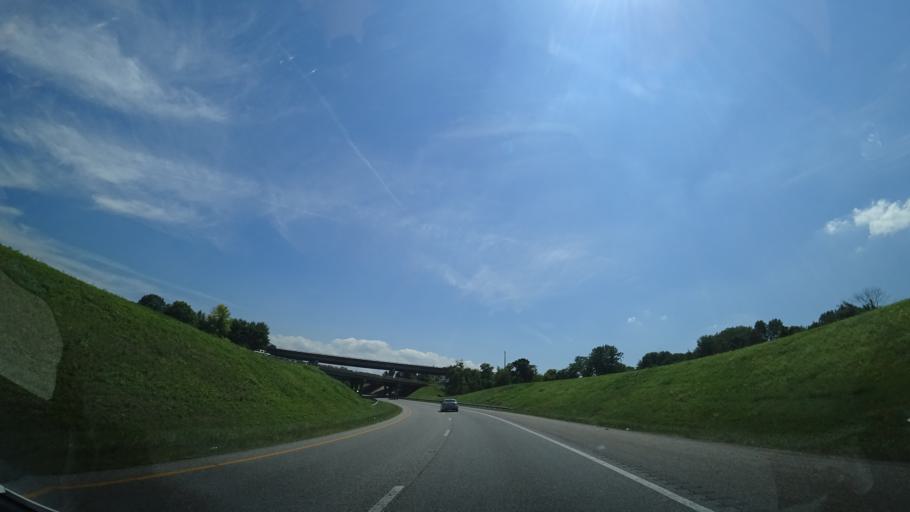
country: US
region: Virginia
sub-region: Augusta County
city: Jolivue
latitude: 38.1228
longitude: -79.0474
